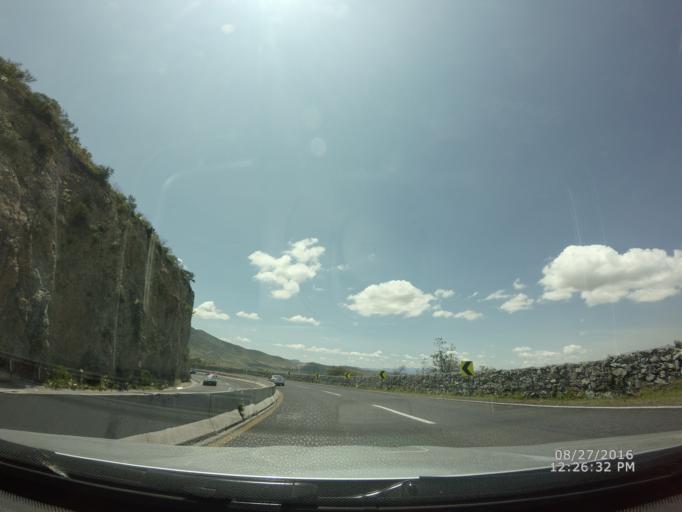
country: MX
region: Hidalgo
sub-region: Mineral de la Reforma
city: Guadalupe Minerva
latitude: 20.1275
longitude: -98.6997
